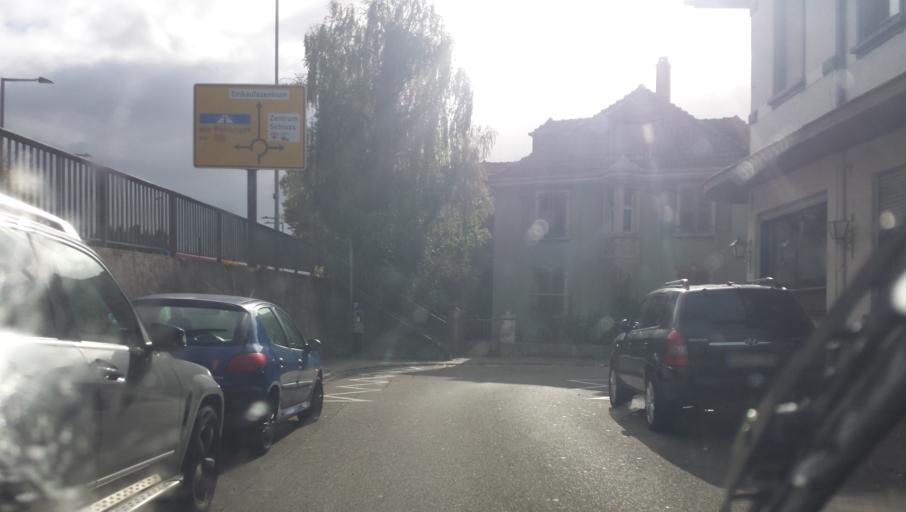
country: DE
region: Baden-Wuerttemberg
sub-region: Karlsruhe Region
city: Schwetzingen
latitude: 49.3865
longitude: 8.5754
